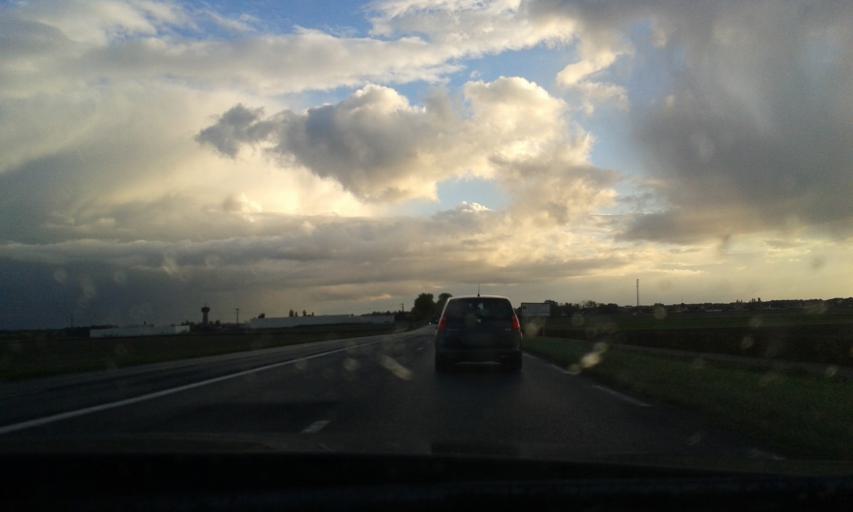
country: FR
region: Centre
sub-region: Departement du Loiret
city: Chevilly
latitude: 48.0426
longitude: 1.8741
